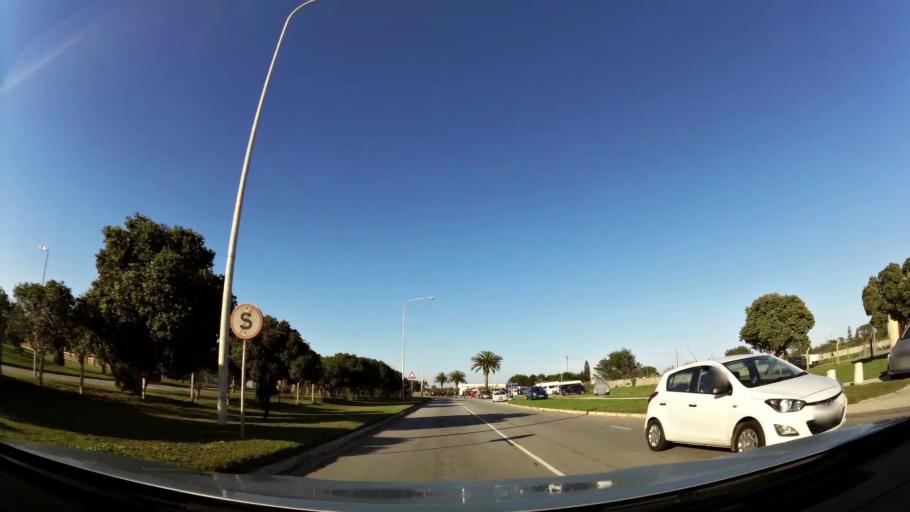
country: ZA
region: Eastern Cape
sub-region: Nelson Mandela Bay Metropolitan Municipality
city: Port Elizabeth
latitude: -33.9988
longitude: 25.6701
